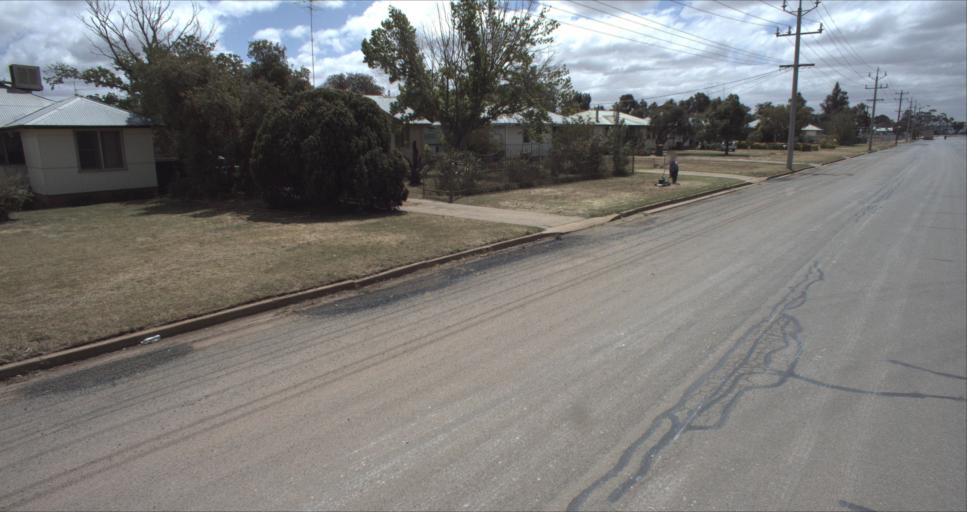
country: AU
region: New South Wales
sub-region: Leeton
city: Leeton
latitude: -34.5575
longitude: 146.3919
